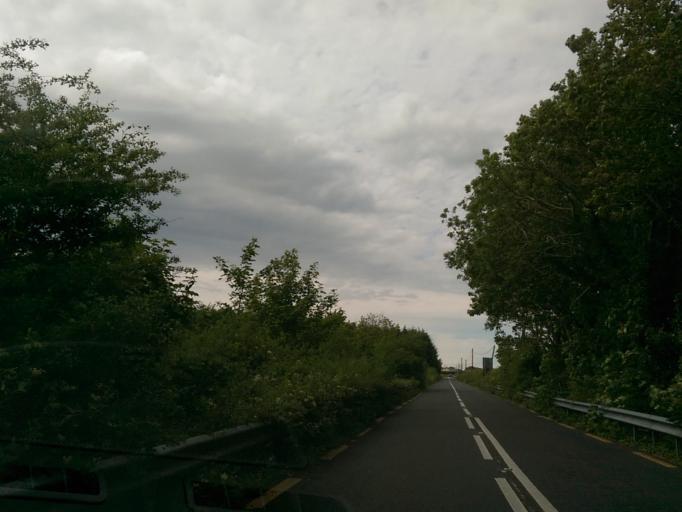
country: IE
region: Connaught
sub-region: County Galway
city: Bearna
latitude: 52.9969
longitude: -9.3078
